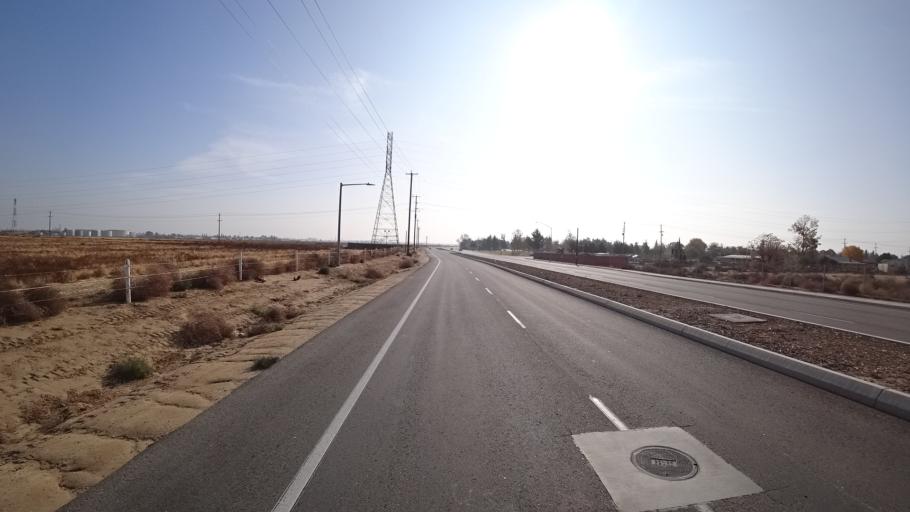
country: US
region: California
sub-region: Kern County
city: Greenacres
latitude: 35.3989
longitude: -119.0654
